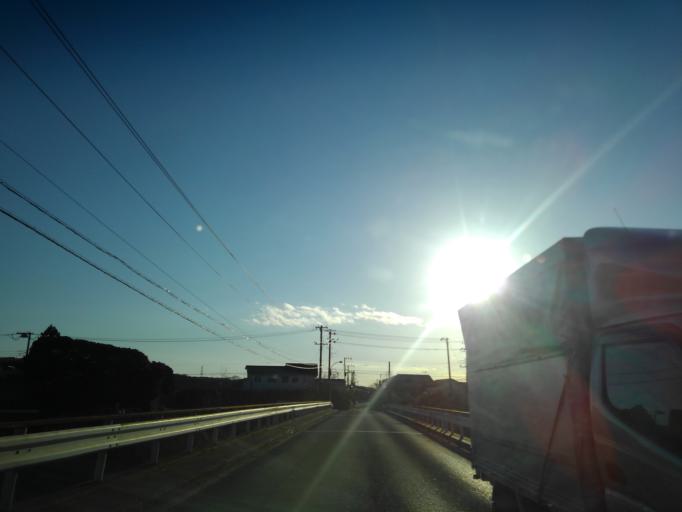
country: JP
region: Chiba
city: Kimitsu
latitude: 35.3254
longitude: 139.8958
